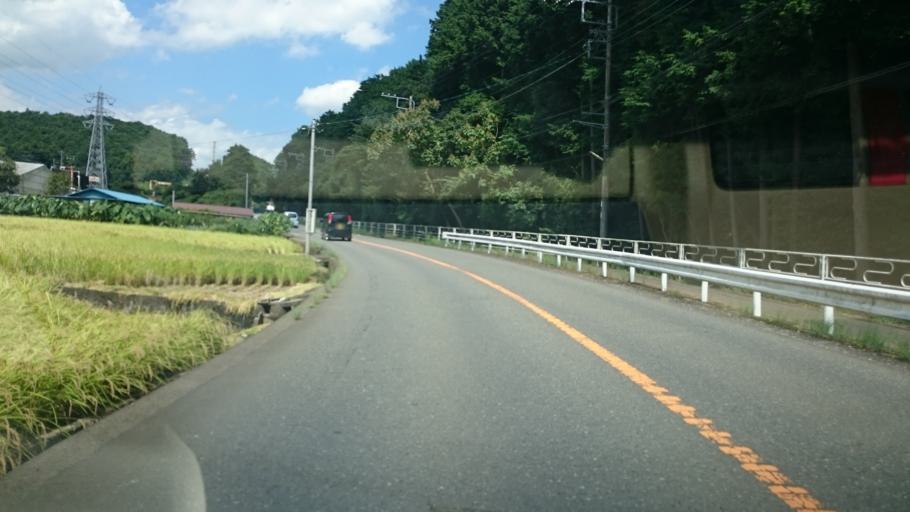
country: JP
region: Shizuoka
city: Mishima
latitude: 35.1996
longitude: 138.9250
